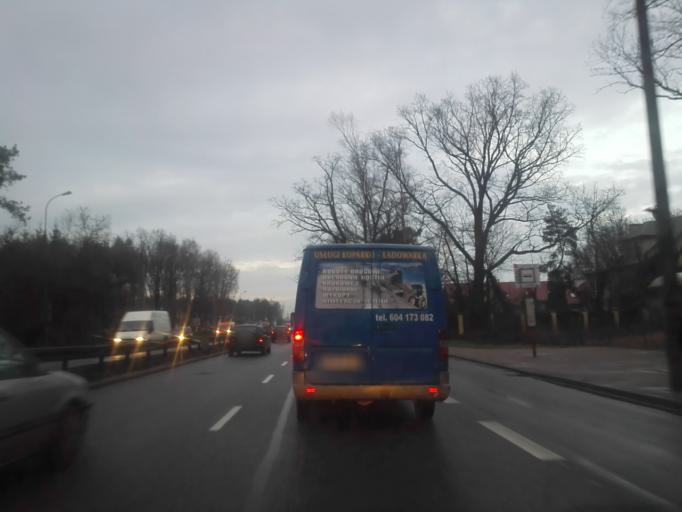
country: PL
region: Masovian Voivodeship
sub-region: Powiat wolominski
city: Slupno
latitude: 52.3529
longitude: 21.1299
